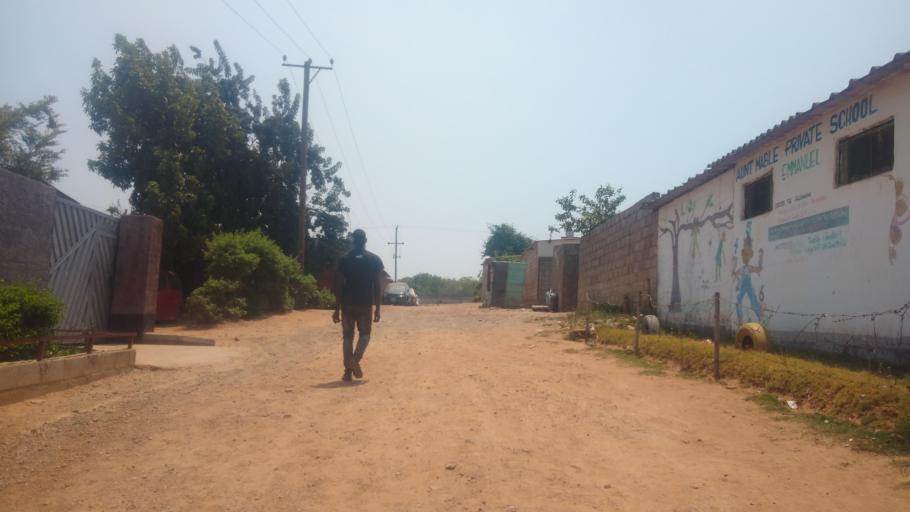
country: ZM
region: Lusaka
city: Lusaka
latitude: -15.4380
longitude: 28.3817
